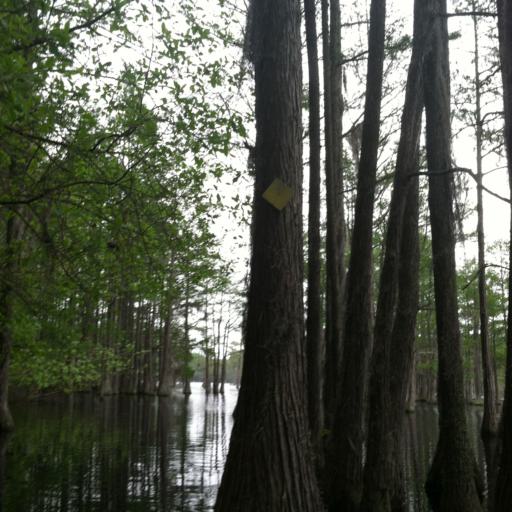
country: US
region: Georgia
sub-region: Emanuel County
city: Twin City
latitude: 32.5495
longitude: -82.1239
